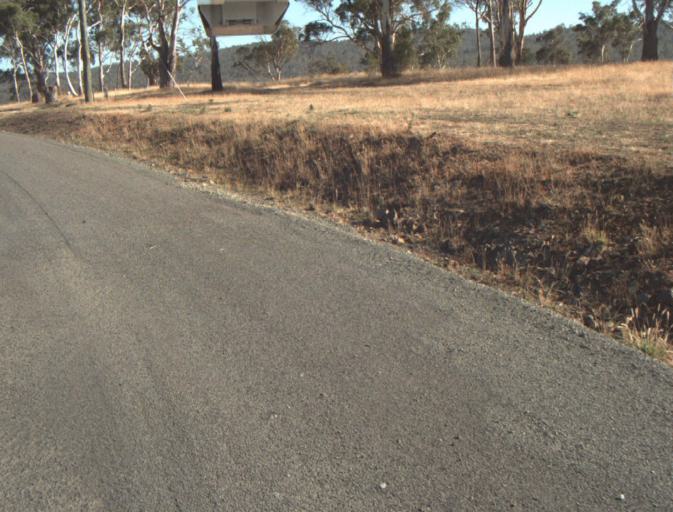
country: AU
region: Tasmania
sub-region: Launceston
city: Newstead
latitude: -41.4387
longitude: 147.2316
